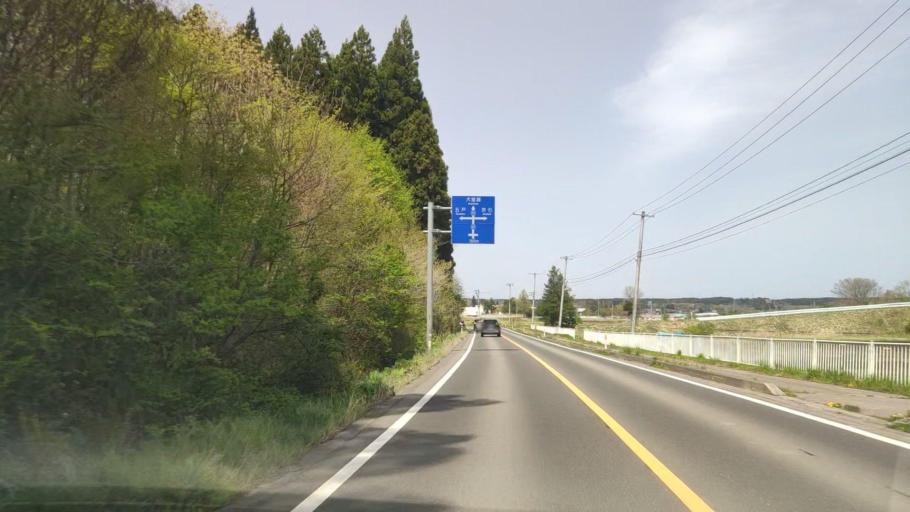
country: JP
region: Aomori
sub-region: Misawa Shi
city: Inuotose
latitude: 40.5850
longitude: 141.3556
